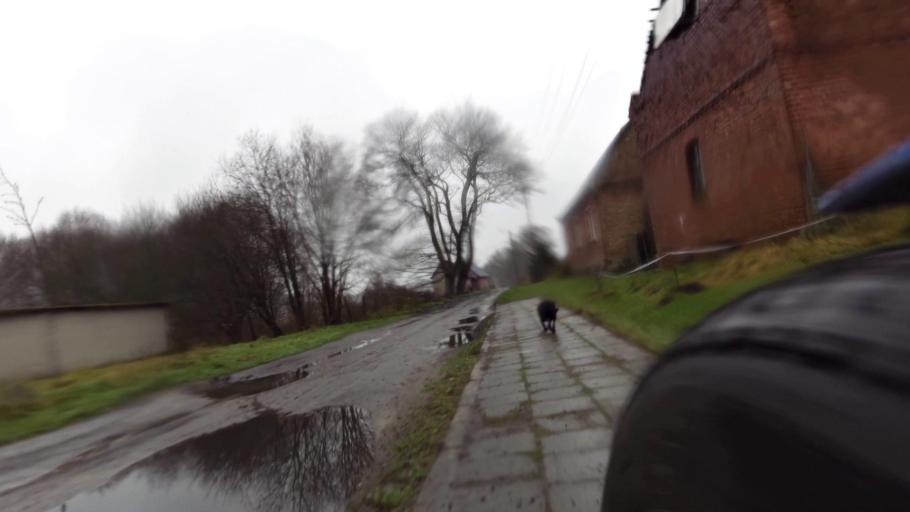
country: PL
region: West Pomeranian Voivodeship
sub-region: Powiat drawski
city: Zlocieniec
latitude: 53.5442
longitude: 15.9528
